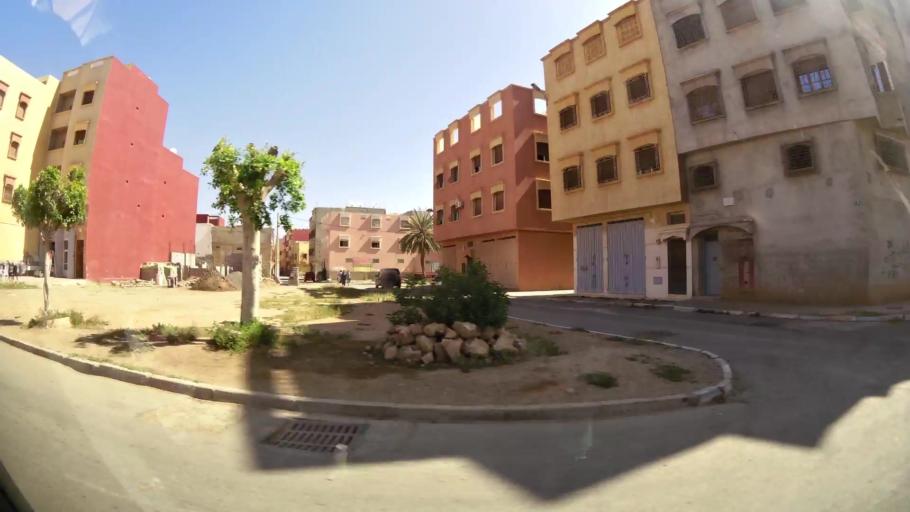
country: MA
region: Souss-Massa-Draa
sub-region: Inezgane-Ait Mellou
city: Inezgane
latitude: 30.3391
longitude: -9.5055
